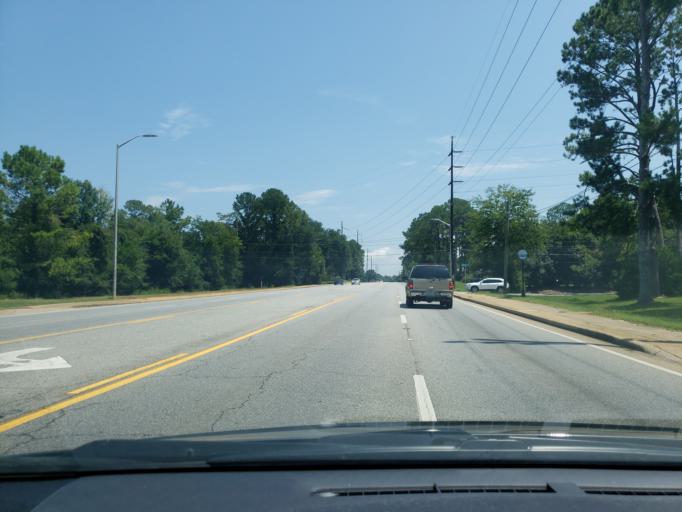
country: US
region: Georgia
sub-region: Dougherty County
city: Albany
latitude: 31.5813
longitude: -84.1973
